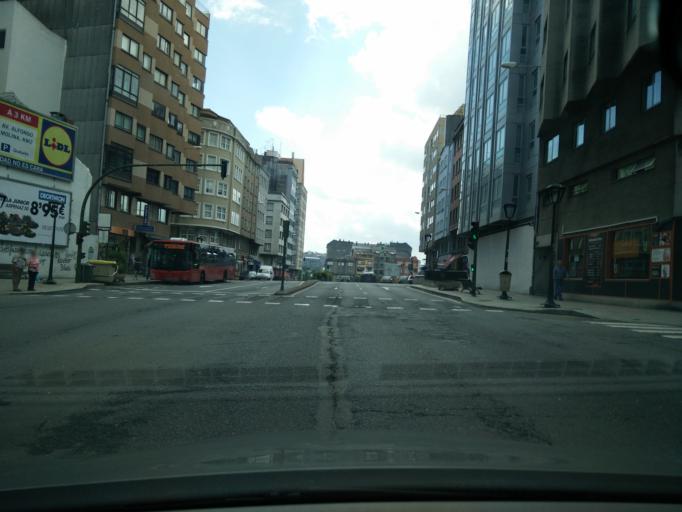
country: ES
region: Galicia
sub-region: Provincia da Coruna
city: A Coruna
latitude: 43.3545
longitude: -8.4105
